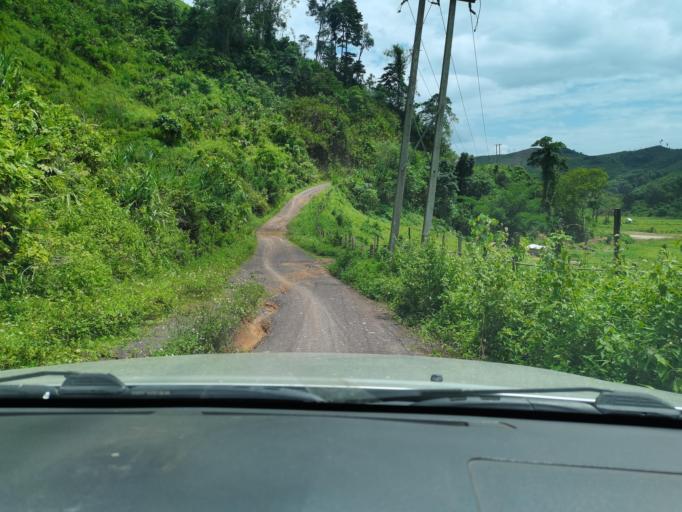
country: LA
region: Loungnamtha
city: Muang Long
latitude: 20.7116
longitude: 101.0124
